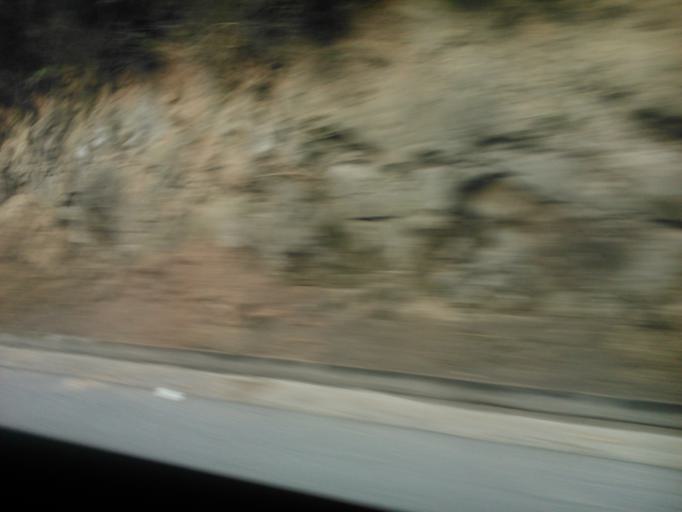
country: CL
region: Maule
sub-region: Provincia de Talca
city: Talca
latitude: -35.3520
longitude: -71.5759
